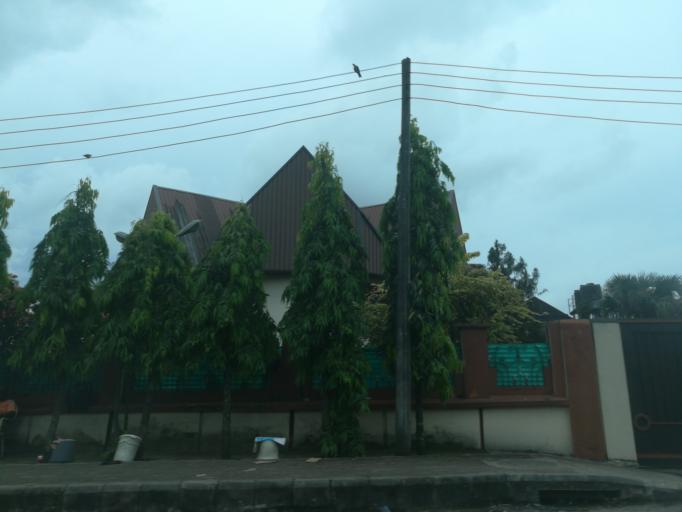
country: NG
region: Rivers
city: Port Harcourt
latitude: 4.8194
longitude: 6.9962
